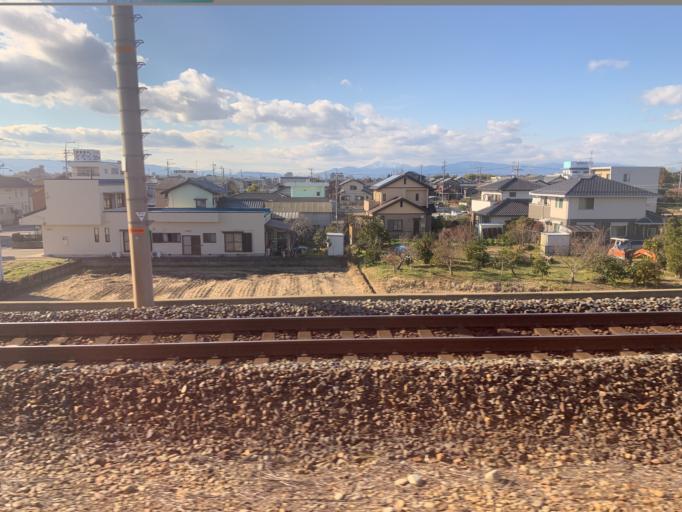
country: JP
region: Gifu
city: Kasamatsucho
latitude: 35.3631
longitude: 136.7796
